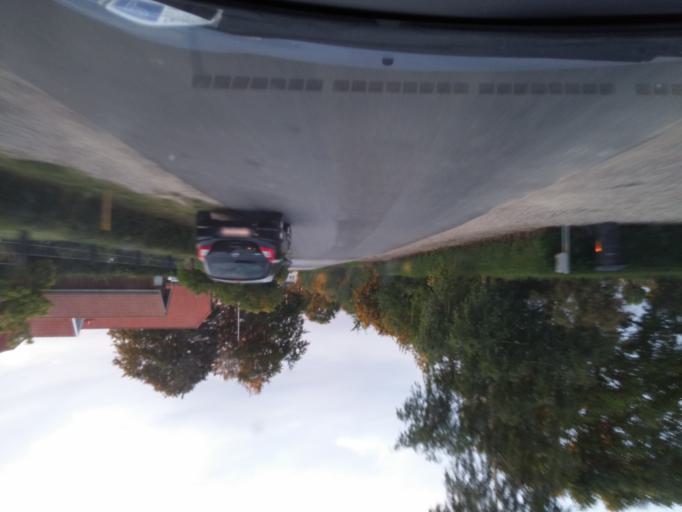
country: DK
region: South Denmark
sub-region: Kerteminde Kommune
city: Munkebo
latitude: 55.4354
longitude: 10.5938
